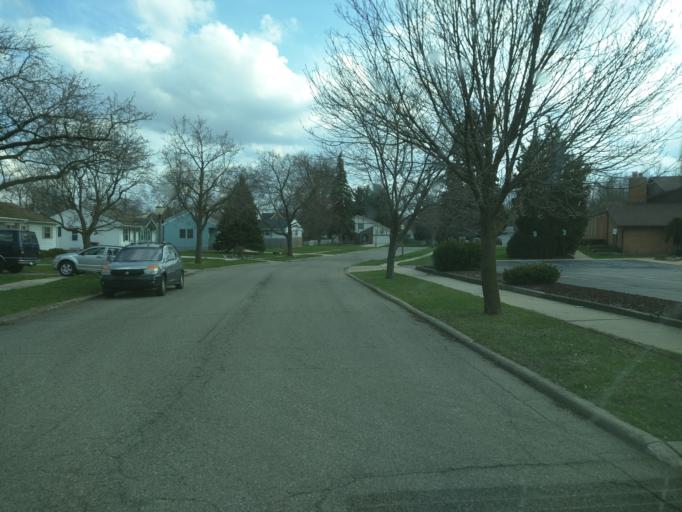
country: US
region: Michigan
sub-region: Ingham County
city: Edgemont Park
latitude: 42.7618
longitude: -84.5924
